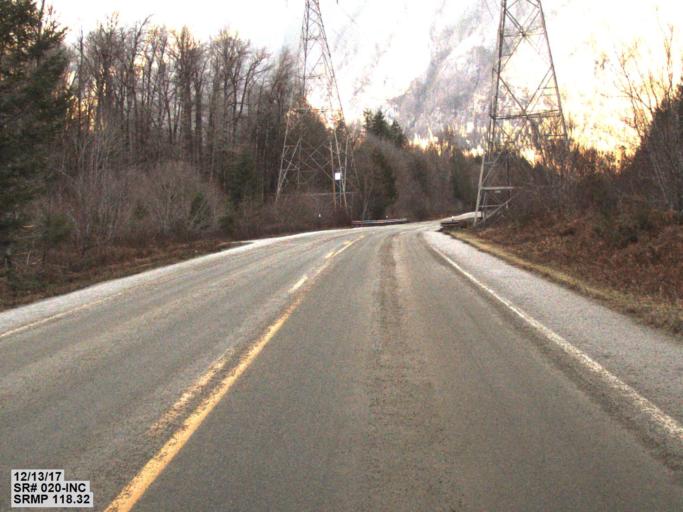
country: US
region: Washington
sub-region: Snohomish County
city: Darrington
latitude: 48.6609
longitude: -121.2881
